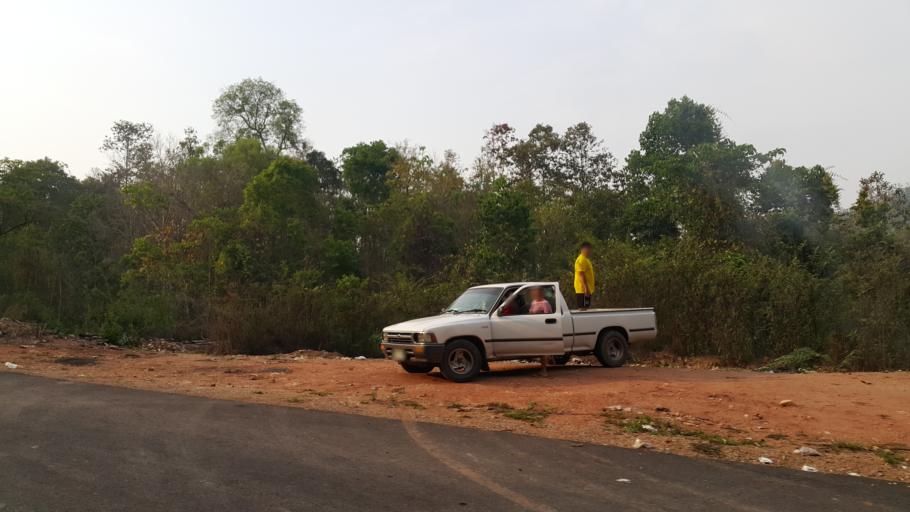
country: TH
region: Chiang Mai
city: Mae On
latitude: 18.7521
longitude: 99.2996
